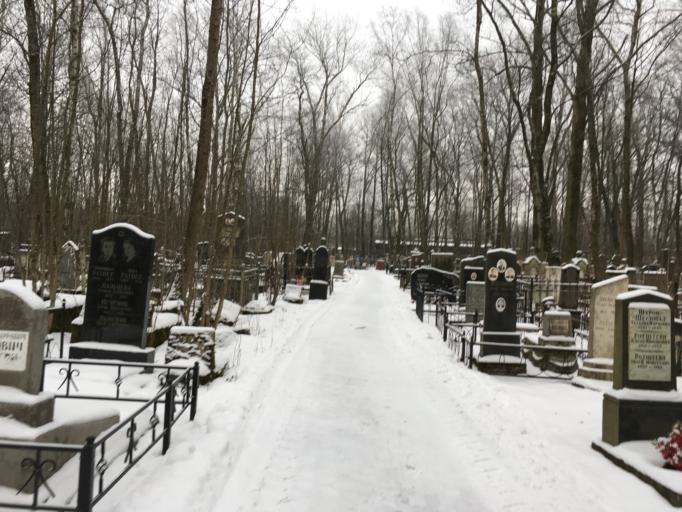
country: RU
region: St.-Petersburg
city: Obukhovo
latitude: 59.8588
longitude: 30.4545
